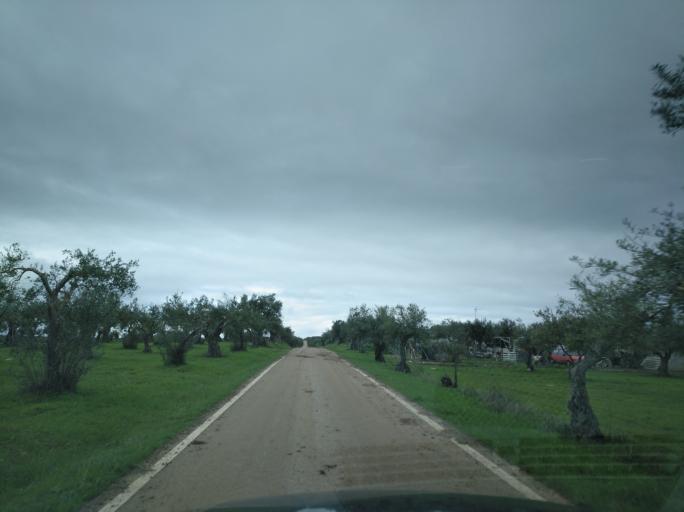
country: PT
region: Portalegre
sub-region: Campo Maior
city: Campo Maior
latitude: 38.9830
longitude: -7.0353
